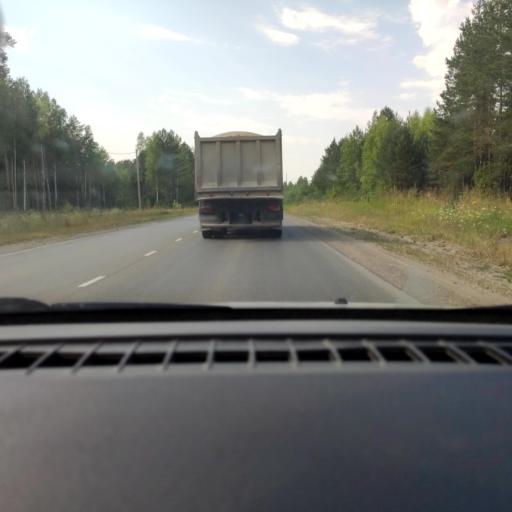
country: RU
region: Perm
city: Overyata
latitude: 58.0184
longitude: 55.8584
